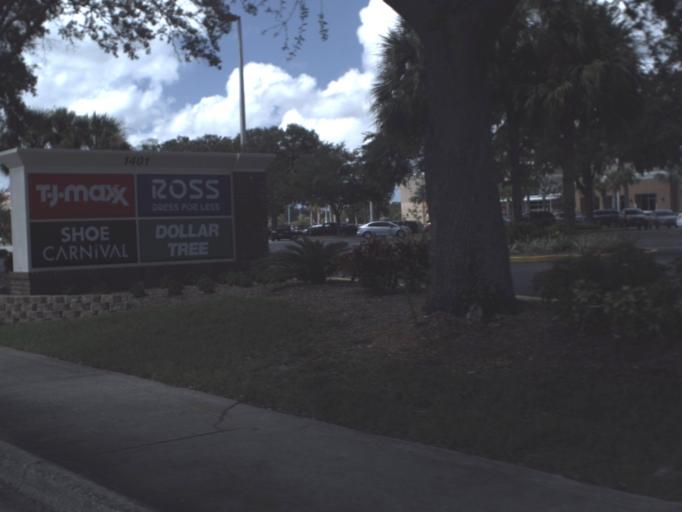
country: US
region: Florida
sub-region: Pinellas County
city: Belleair
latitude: 27.9305
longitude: -82.7877
